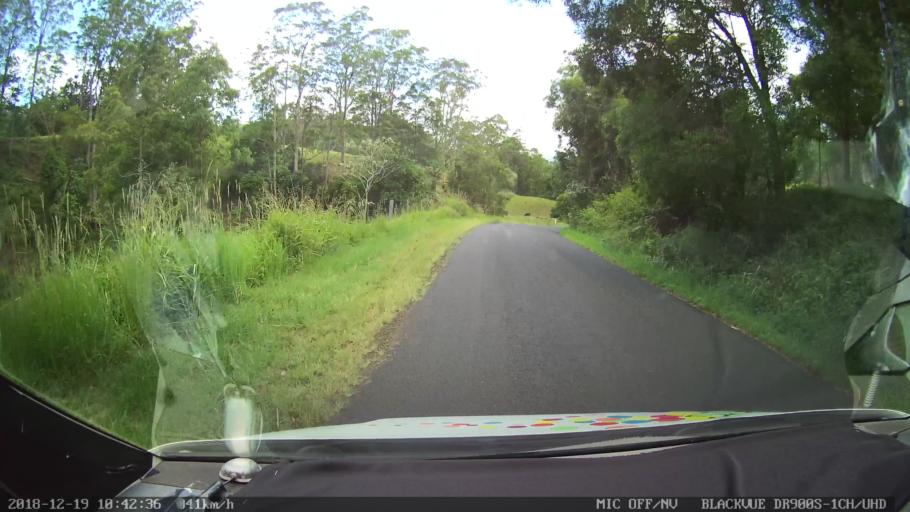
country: AU
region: New South Wales
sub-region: Lismore Municipality
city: Nimbin
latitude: -28.5922
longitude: 153.1684
